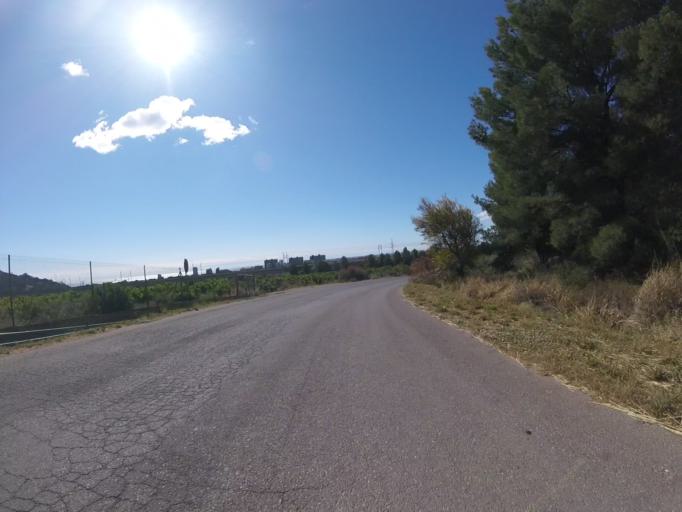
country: ES
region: Valencia
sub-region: Provincia de Castello
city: Benicassim
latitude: 40.0644
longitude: 0.0718
